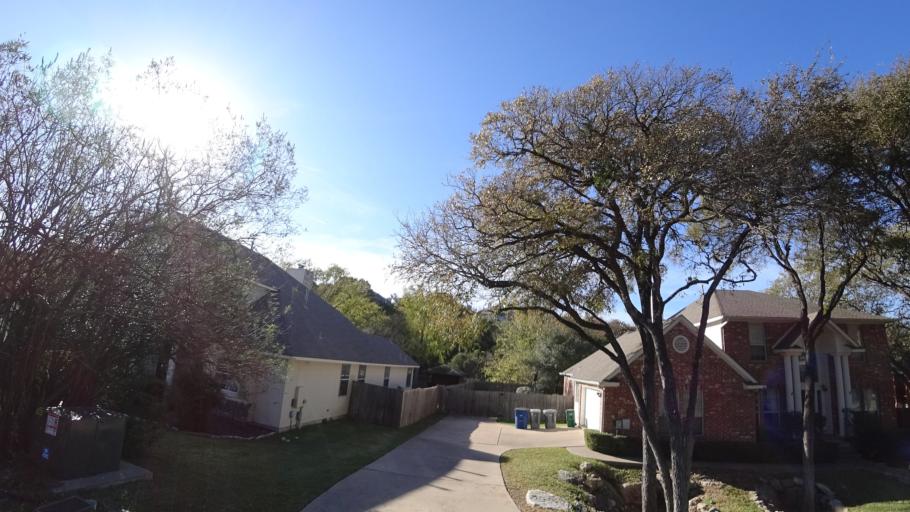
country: US
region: Texas
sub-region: Williamson County
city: Jollyville
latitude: 30.4184
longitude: -97.7752
